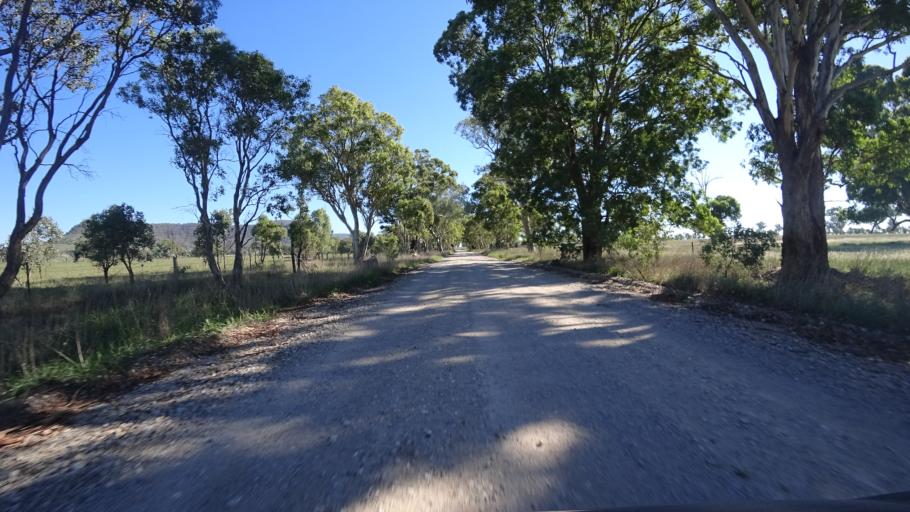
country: AU
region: New South Wales
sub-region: Mid-Western Regional
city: Kandos
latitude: -32.8277
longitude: 150.0187
